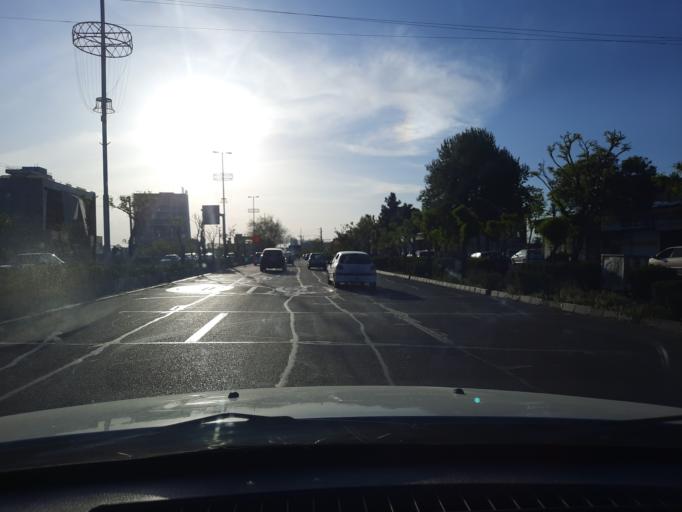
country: IR
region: Qazvin
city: Qazvin
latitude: 36.2637
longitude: 50.0355
